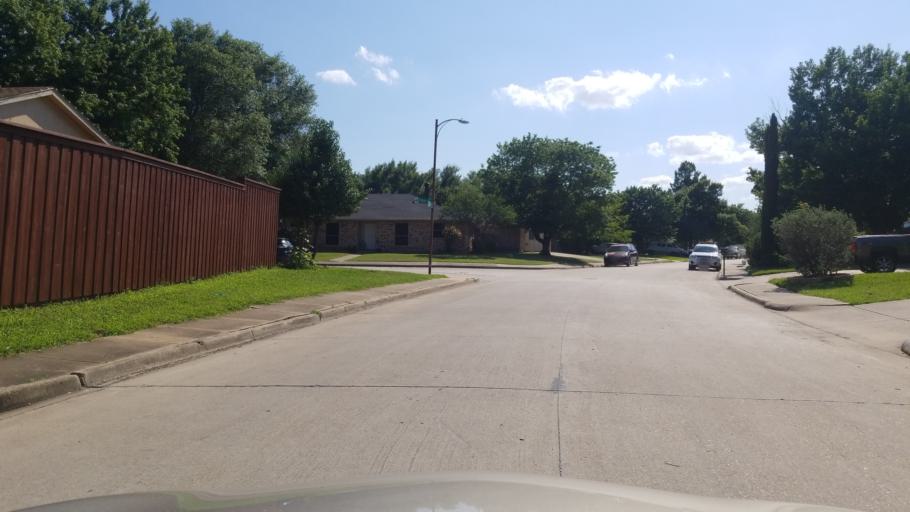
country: US
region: Texas
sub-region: Dallas County
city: Grand Prairie
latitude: 32.6877
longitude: -97.0147
